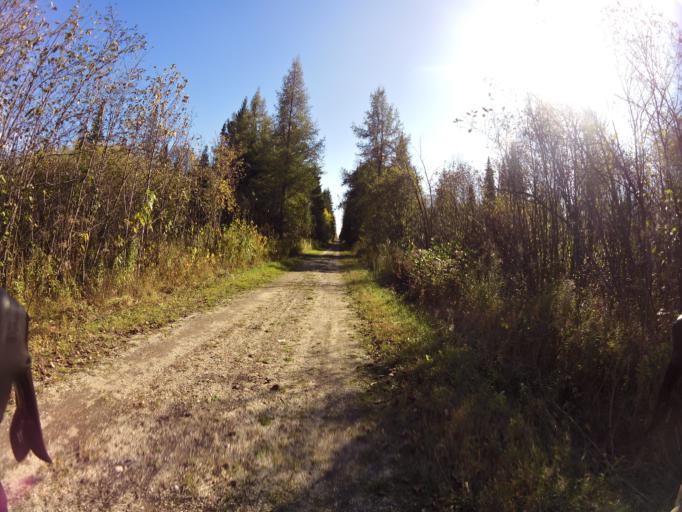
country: CA
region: Quebec
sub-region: Outaouais
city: Wakefield
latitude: 45.8875
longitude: -76.0324
